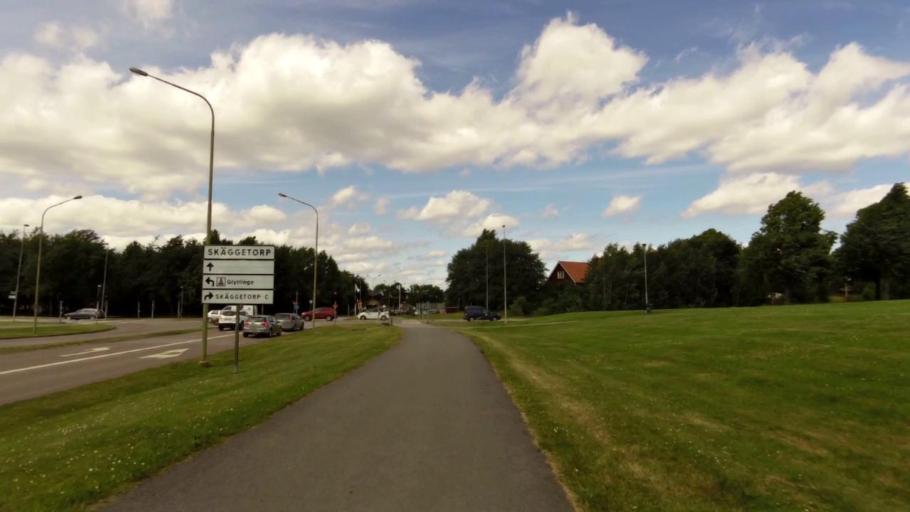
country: SE
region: OEstergoetland
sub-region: Linkopings Kommun
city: Linkoping
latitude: 58.4209
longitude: 15.5870
